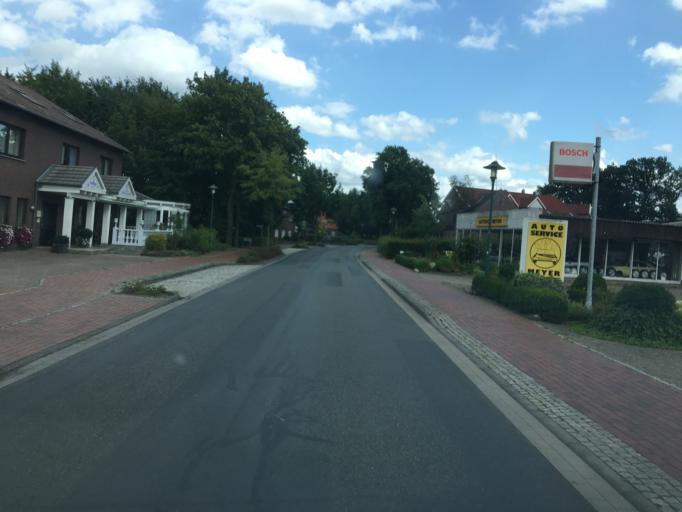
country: DE
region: Lower Saxony
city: Hilkenbrook
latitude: 53.0718
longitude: 7.7006
